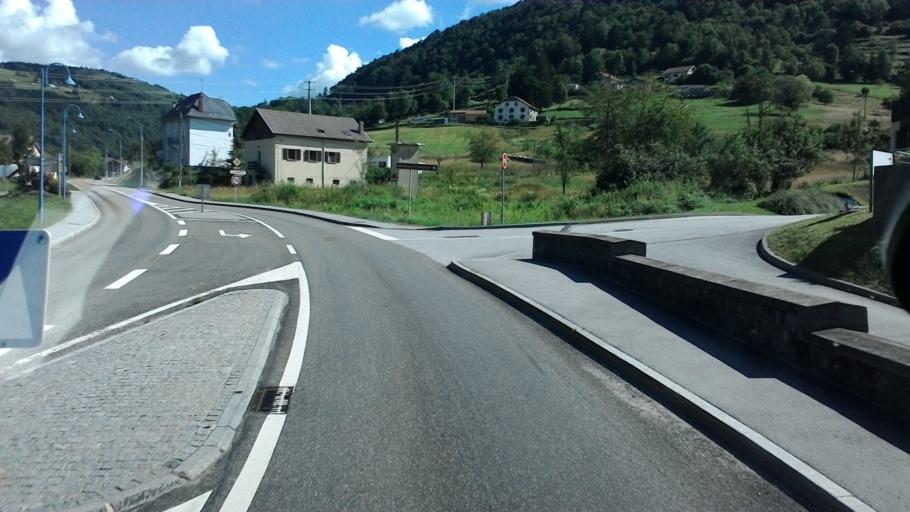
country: FR
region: Lorraine
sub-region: Departement des Vosges
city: Cornimont
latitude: 47.9735
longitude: 6.8318
